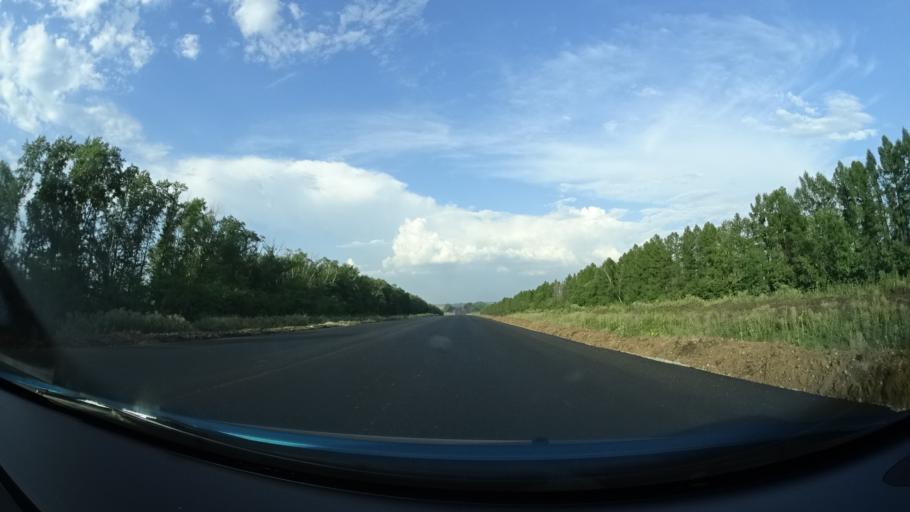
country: RU
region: Samara
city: Sukhodol
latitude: 53.7796
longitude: 50.9159
